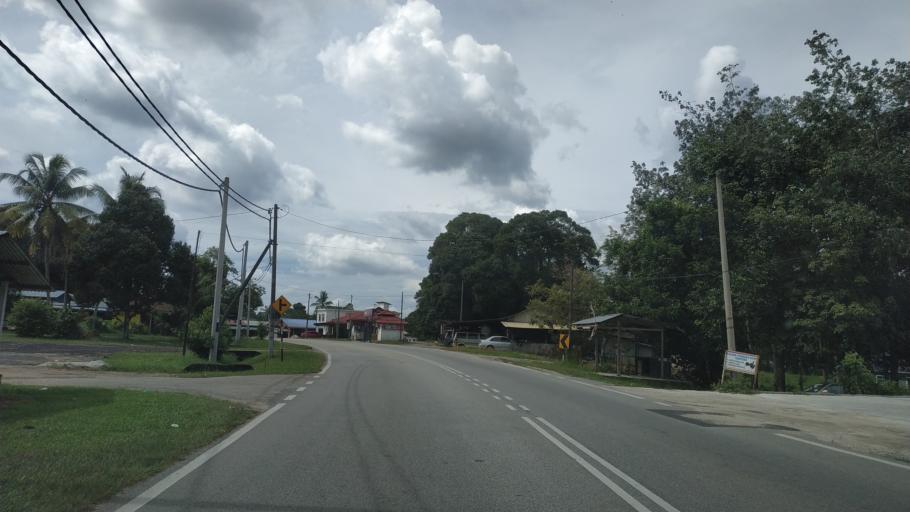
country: MY
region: Kedah
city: Kulim
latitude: 5.4281
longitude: 100.6611
